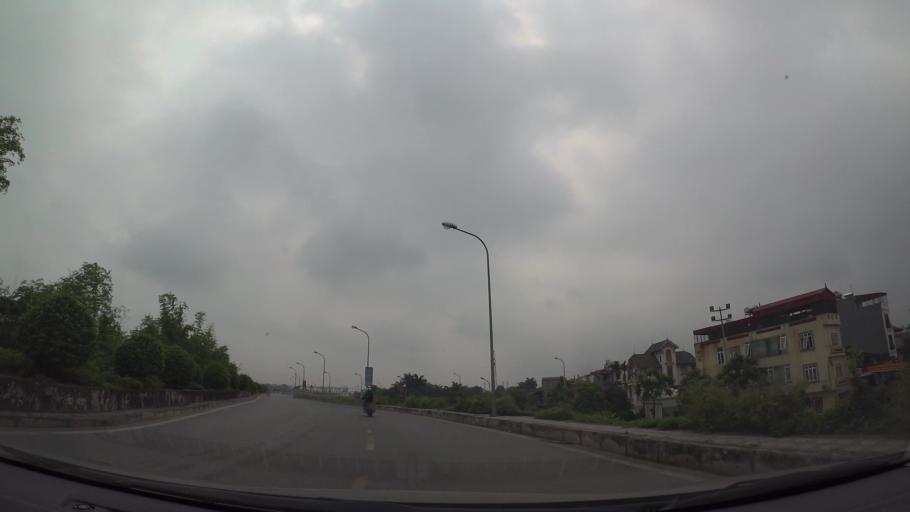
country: VN
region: Ha Noi
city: Trau Quy
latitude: 21.0768
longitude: 105.9020
